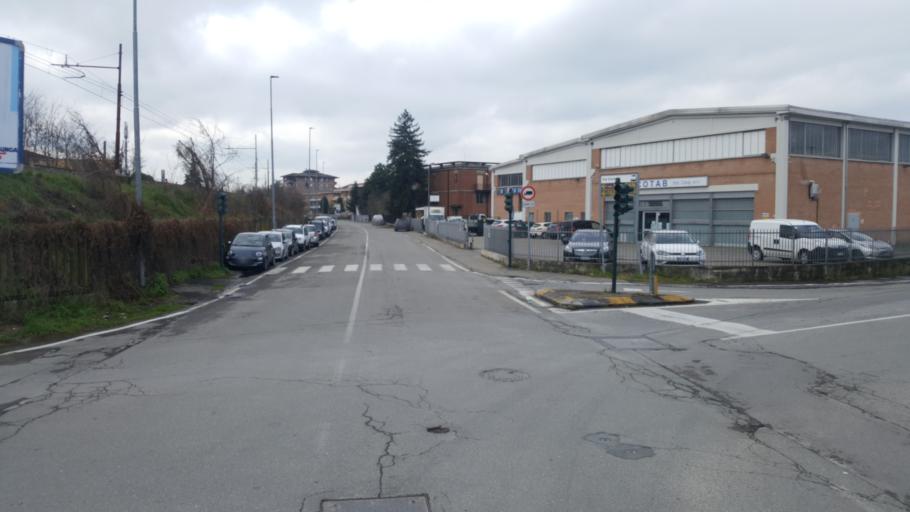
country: IT
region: Emilia-Romagna
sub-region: Provincia di Parma
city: Parma
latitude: 44.8099
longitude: 10.3064
